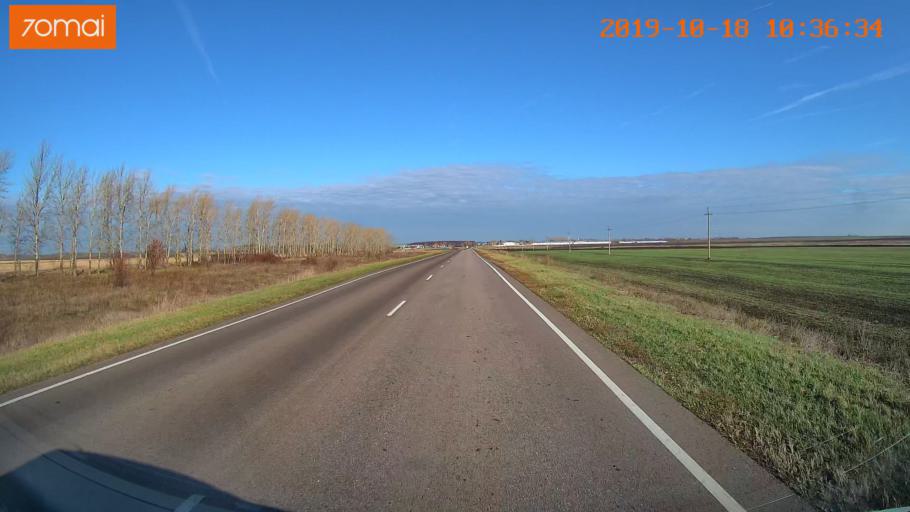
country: RU
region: Tula
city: Kurkino
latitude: 53.5502
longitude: 38.6265
